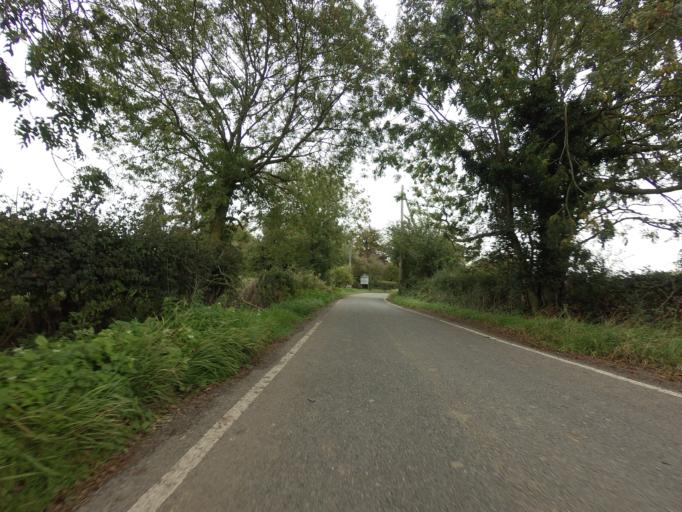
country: GB
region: England
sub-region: Cambridgeshire
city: Duxford
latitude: 51.9957
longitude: 0.1010
